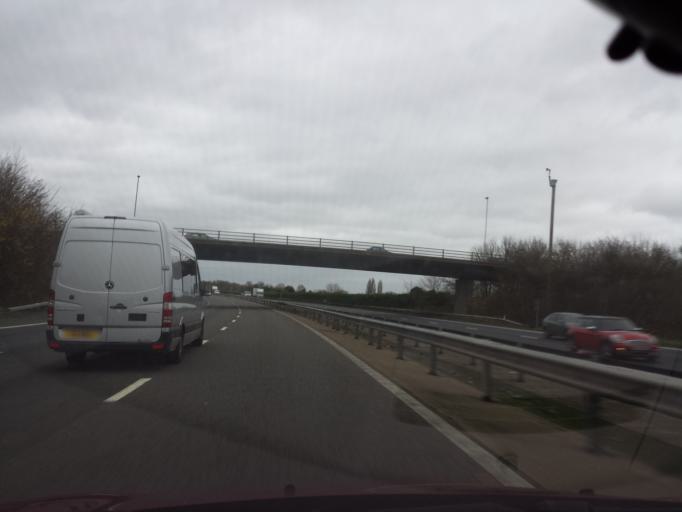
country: GB
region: England
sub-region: Surrey
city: Shepperton
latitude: 51.3972
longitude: -0.4542
